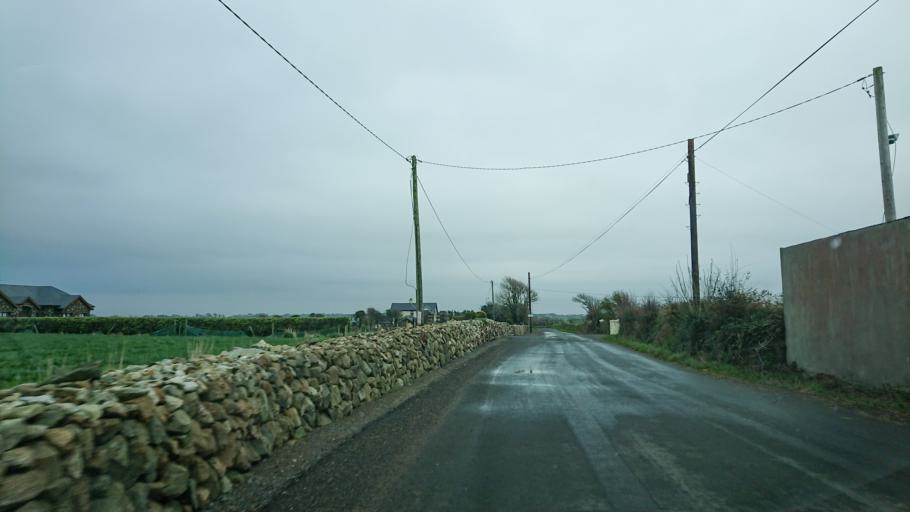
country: IE
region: Munster
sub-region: Waterford
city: Tra Mhor
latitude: 52.1411
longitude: -7.2163
